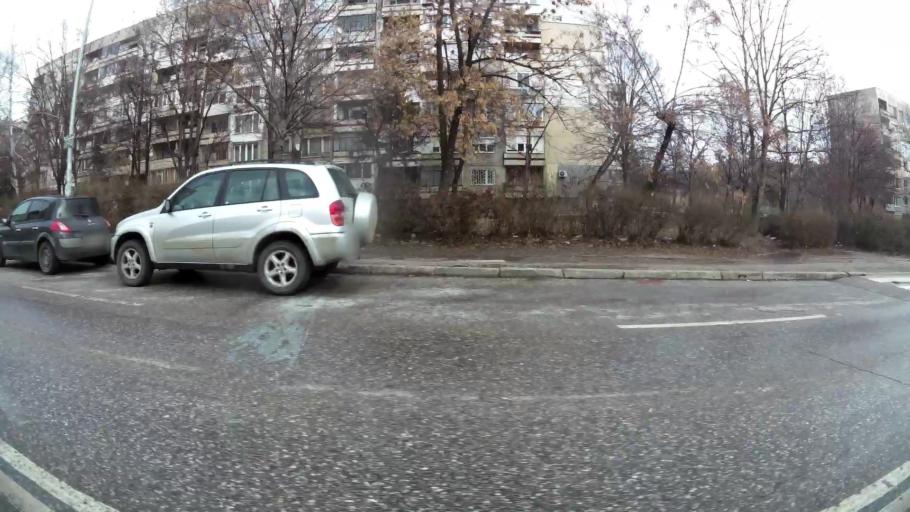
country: BG
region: Sofiya
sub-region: Obshtina Bozhurishte
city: Bozhurishte
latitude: 42.7180
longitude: 23.2404
